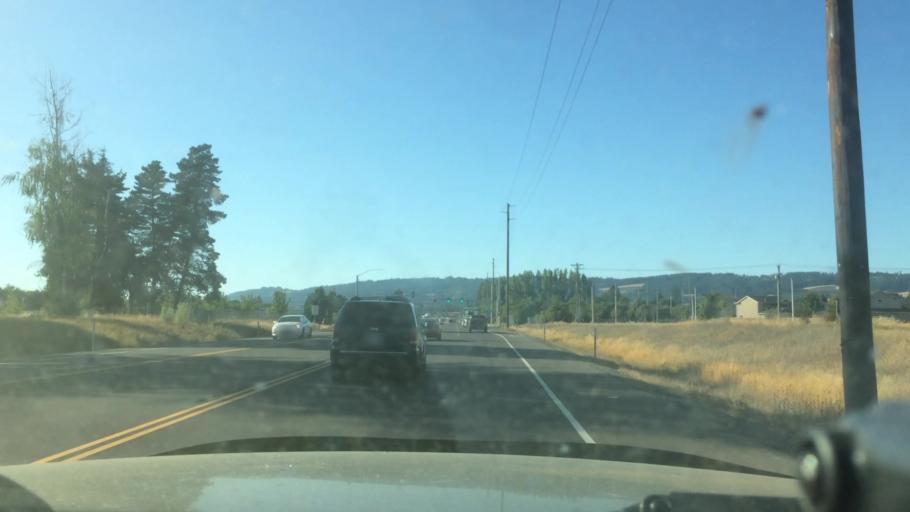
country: US
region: Oregon
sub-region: Yamhill County
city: Newberg
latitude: 45.2886
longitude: -122.9466
